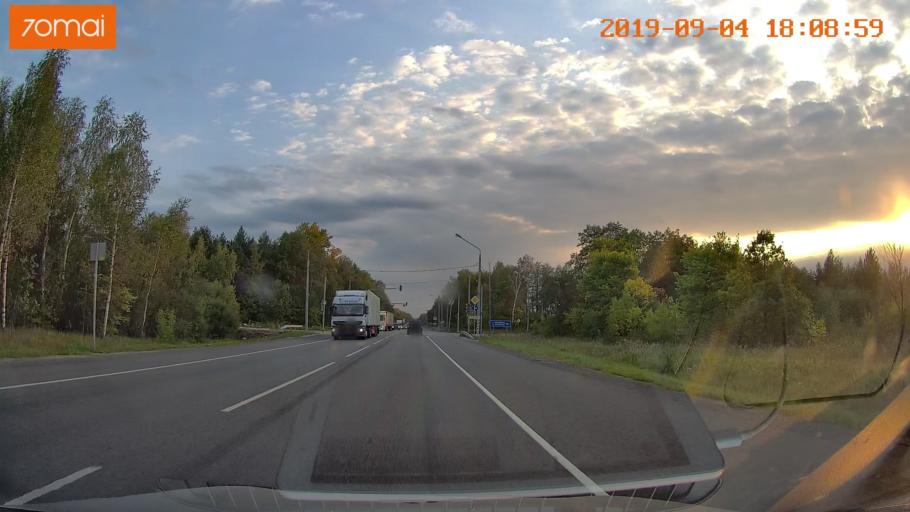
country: RU
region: Moskovskaya
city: Khorlovo
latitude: 55.3998
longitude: 38.7790
